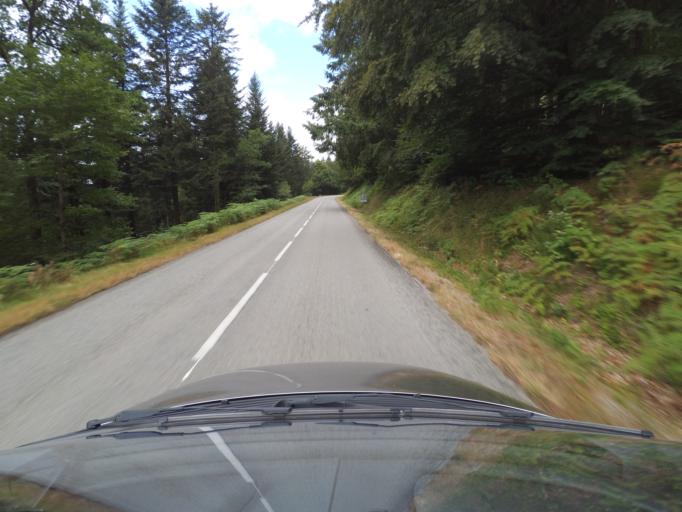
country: FR
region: Limousin
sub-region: Departement de la Creuse
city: Bourganeuf
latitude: 45.9063
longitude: 1.8584
